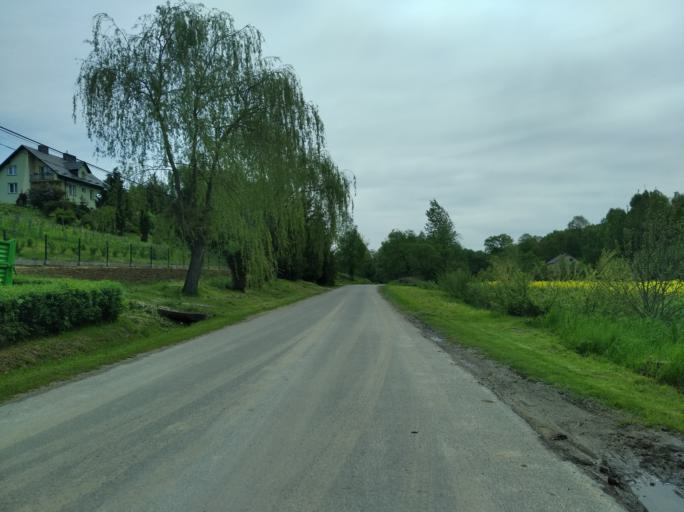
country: PL
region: Subcarpathian Voivodeship
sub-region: Powiat strzyzowski
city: Strzyzow
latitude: 49.9273
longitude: 21.7631
